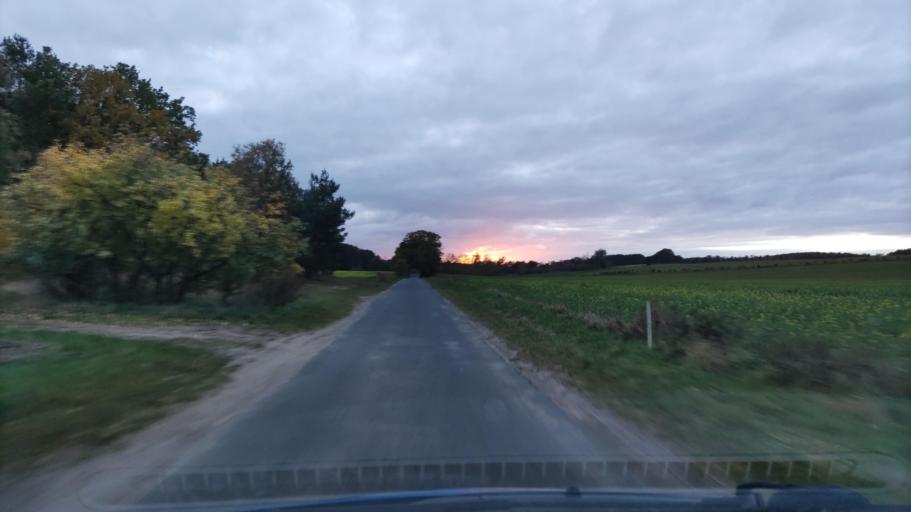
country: DE
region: Lower Saxony
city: Hitzacker
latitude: 53.1398
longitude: 11.0278
